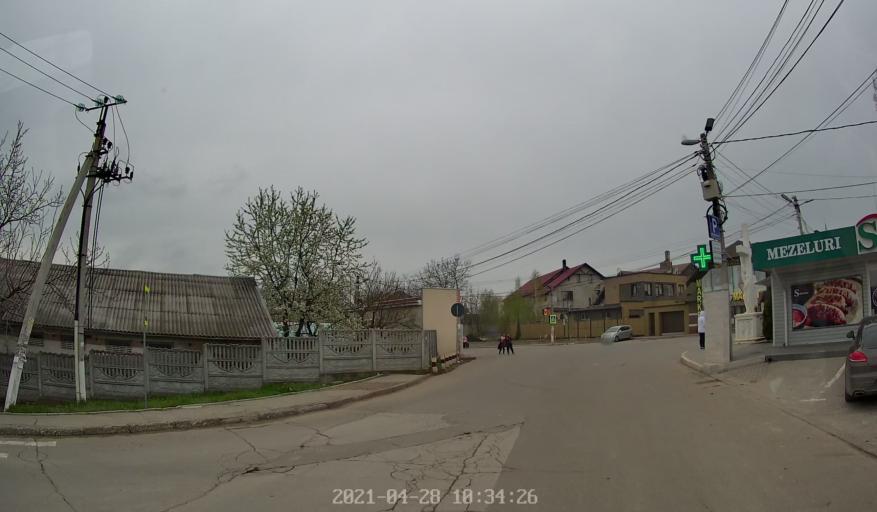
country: MD
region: Chisinau
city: Chisinau
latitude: 46.9845
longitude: 28.9313
